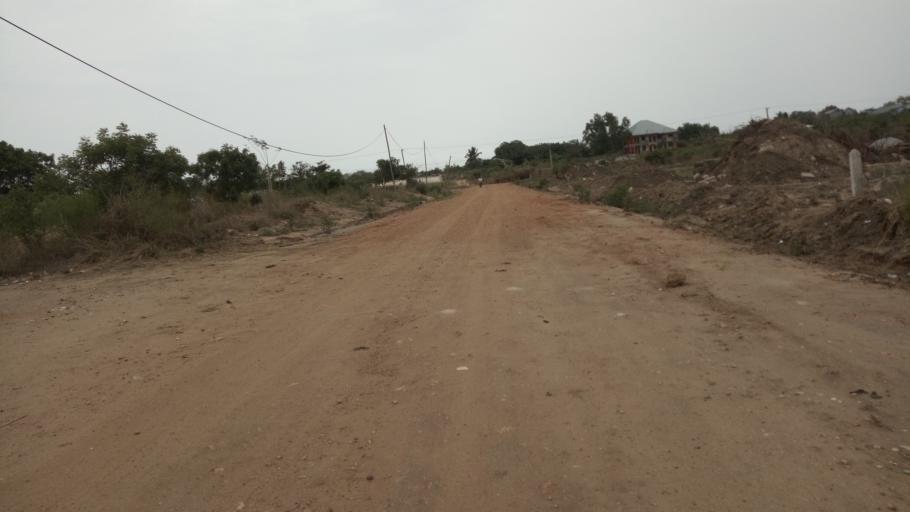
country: GH
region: Central
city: Winneba
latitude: 5.3777
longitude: -0.6381
